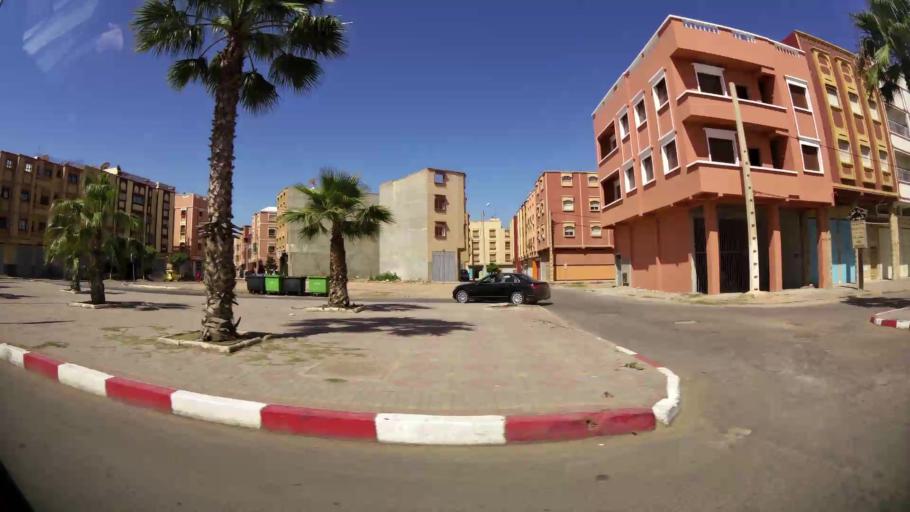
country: MA
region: Souss-Massa-Draa
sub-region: Inezgane-Ait Mellou
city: Inezgane
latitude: 30.3313
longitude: -9.5040
